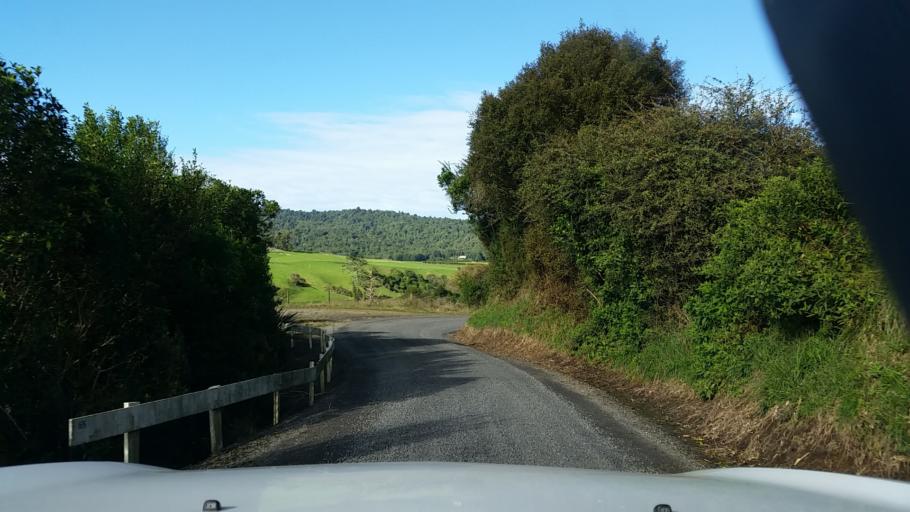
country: NZ
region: Waikato
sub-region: Matamata-Piako District
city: Matamata
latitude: -37.8092
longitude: 175.6347
